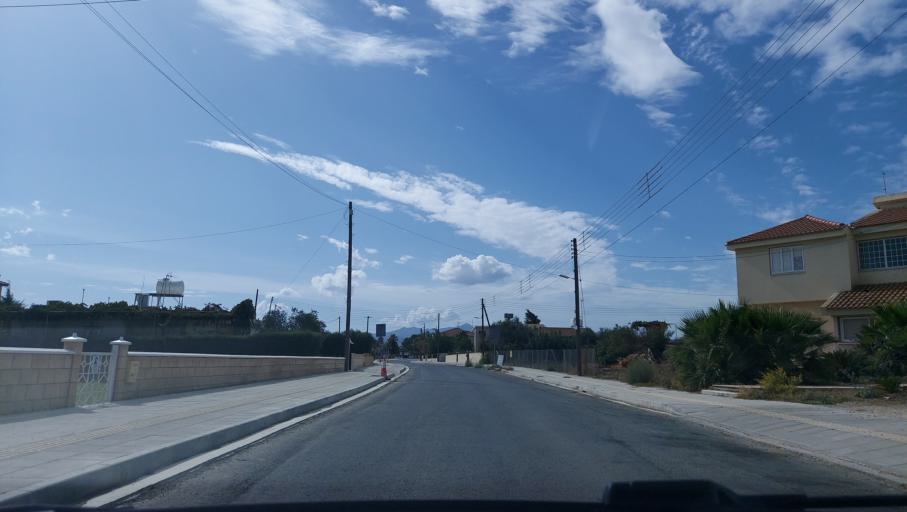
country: CY
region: Lefkosia
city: Pano Deftera
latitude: 35.0731
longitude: 33.2620
